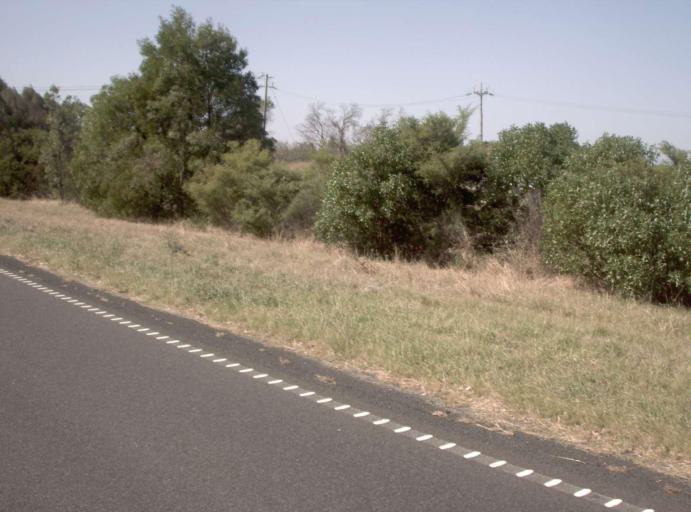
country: AU
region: Victoria
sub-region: Kingston
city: Patterson Lakes
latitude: -38.0617
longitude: 145.1481
